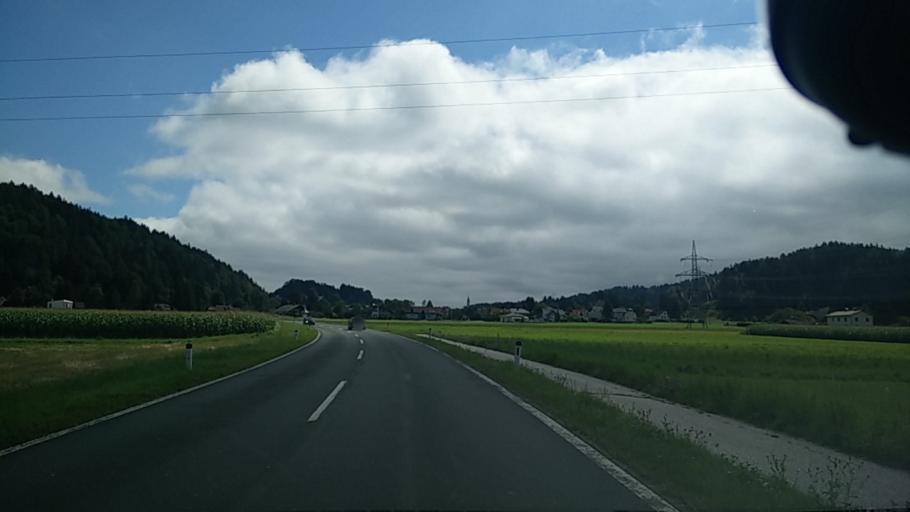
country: AT
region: Carinthia
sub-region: Politischer Bezirk Villach Land
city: Finkenstein am Faaker See
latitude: 46.5592
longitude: 13.9109
